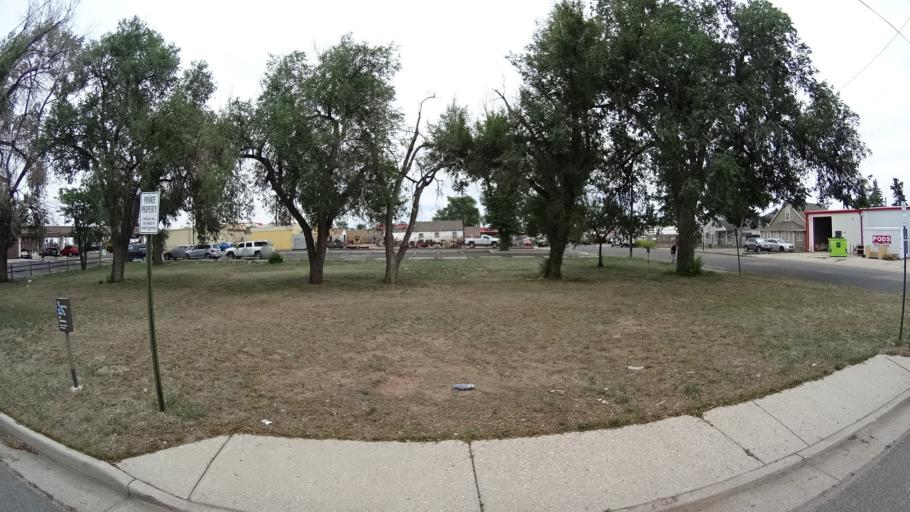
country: US
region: Colorado
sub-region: El Paso County
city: Colorado Springs
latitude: 38.8383
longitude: -104.7775
